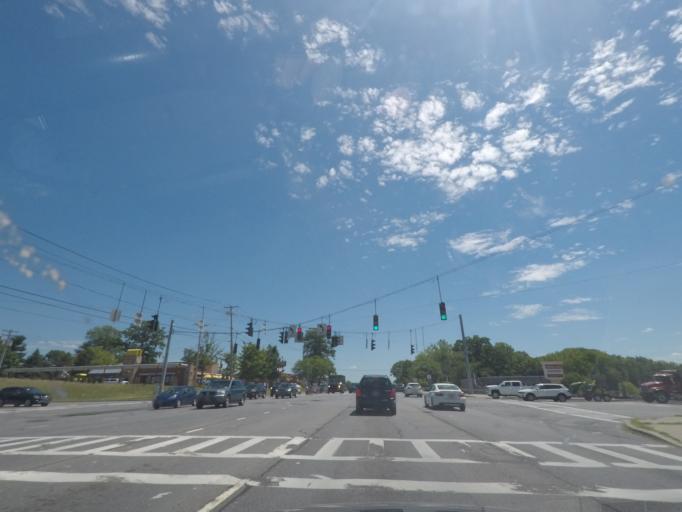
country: US
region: New York
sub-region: Albany County
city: Roessleville
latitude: 42.7563
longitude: -73.7768
